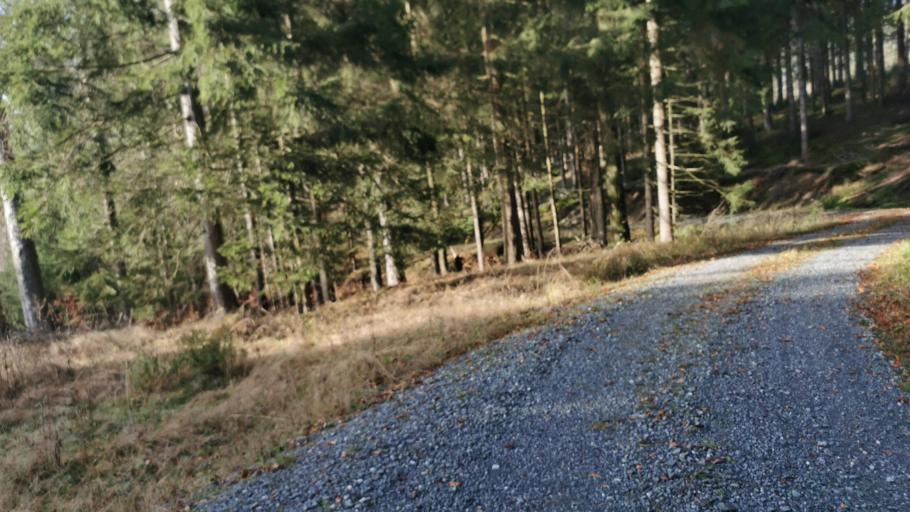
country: DE
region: Bavaria
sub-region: Upper Franconia
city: Tschirn
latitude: 50.4398
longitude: 11.4593
